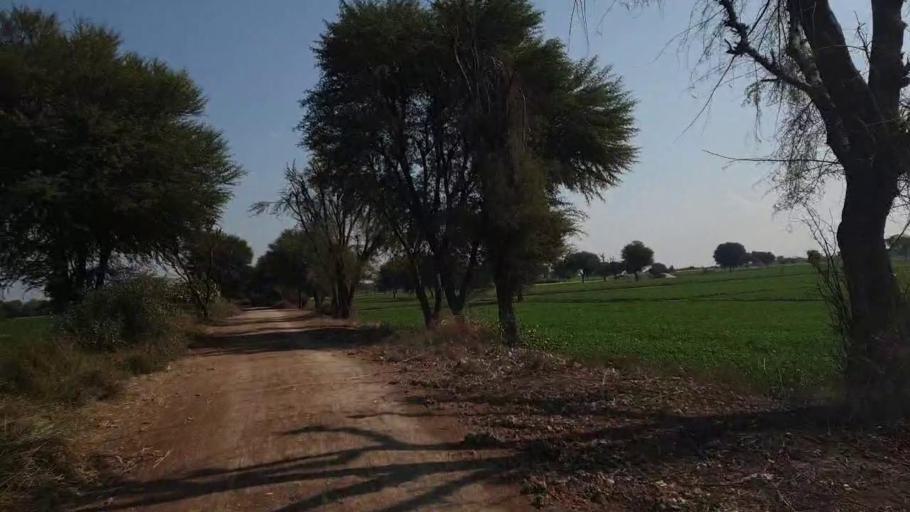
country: PK
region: Sindh
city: Shahpur Chakar
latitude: 26.0513
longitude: 68.5996
